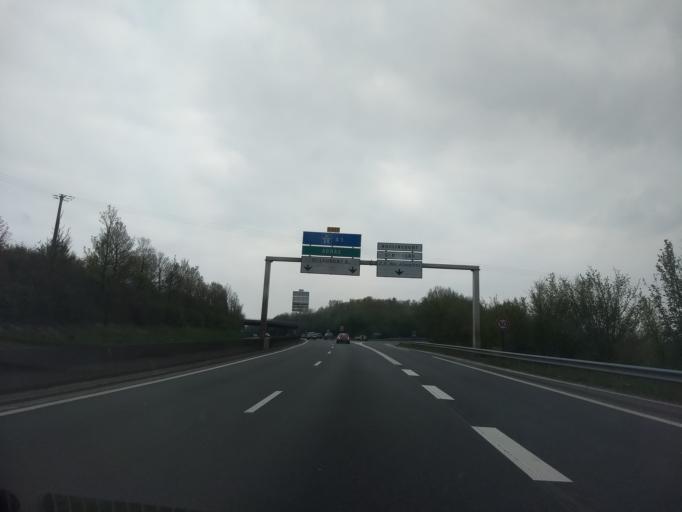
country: FR
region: Nord-Pas-de-Calais
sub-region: Departement du Pas-de-Calais
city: Saint-Nicolas
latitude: 50.3129
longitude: 2.7759
